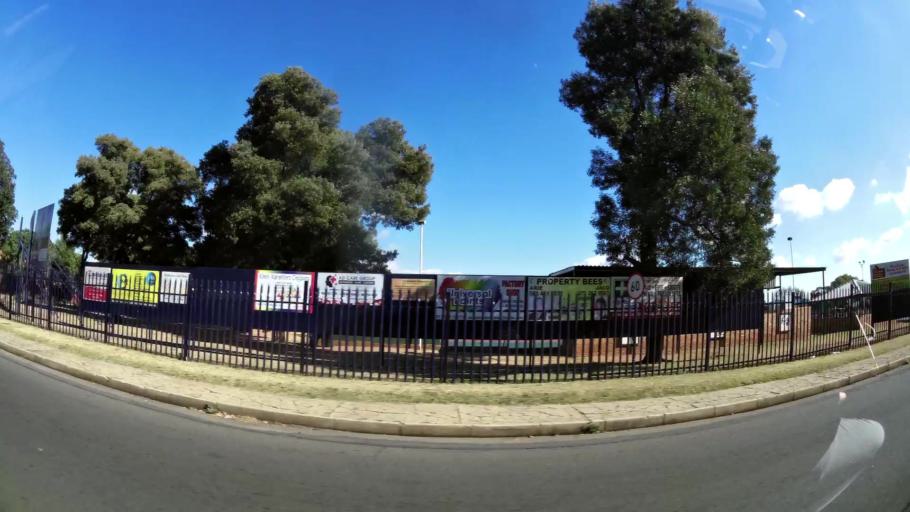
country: ZA
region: Gauteng
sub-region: City of Johannesburg Metropolitan Municipality
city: Roodepoort
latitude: -26.1386
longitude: 27.8363
